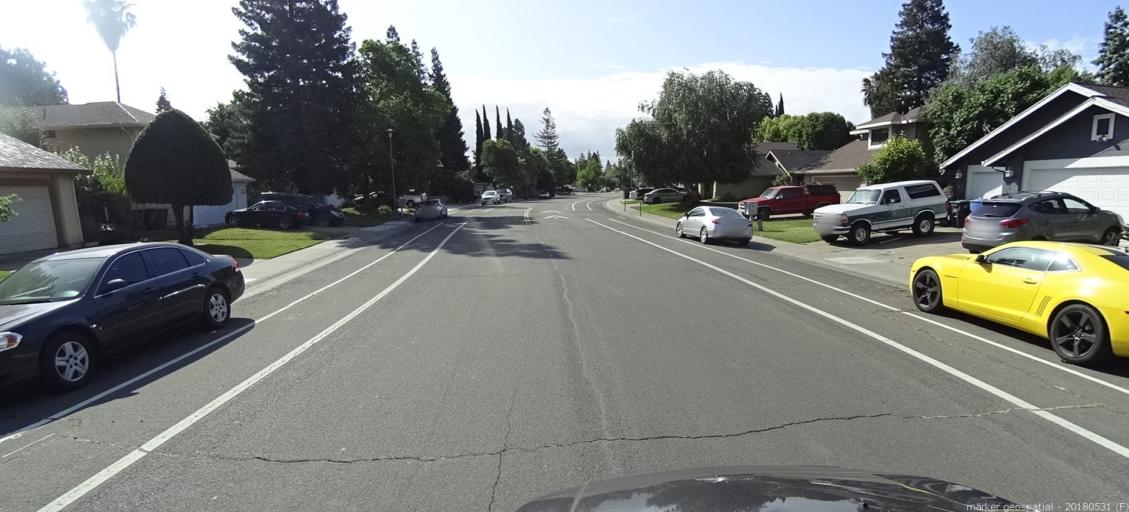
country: US
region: California
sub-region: Sacramento County
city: Sacramento
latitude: 38.6331
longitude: -121.4903
